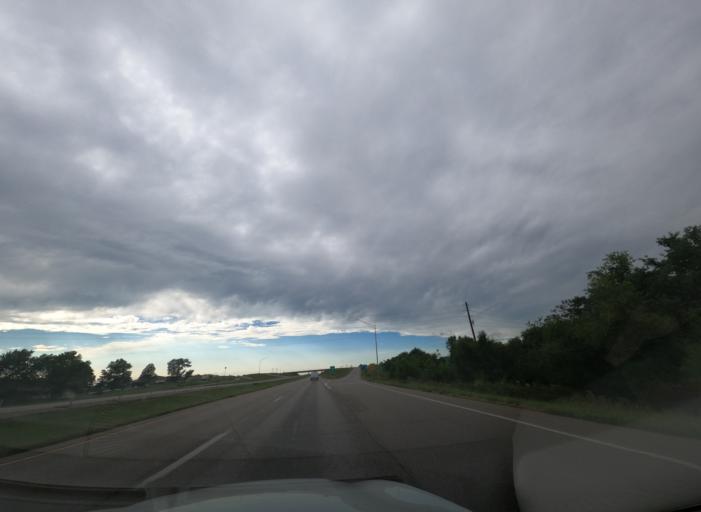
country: US
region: Missouri
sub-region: Sainte Genevieve County
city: Sainte Genevieve
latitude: 37.9331
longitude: -90.1177
